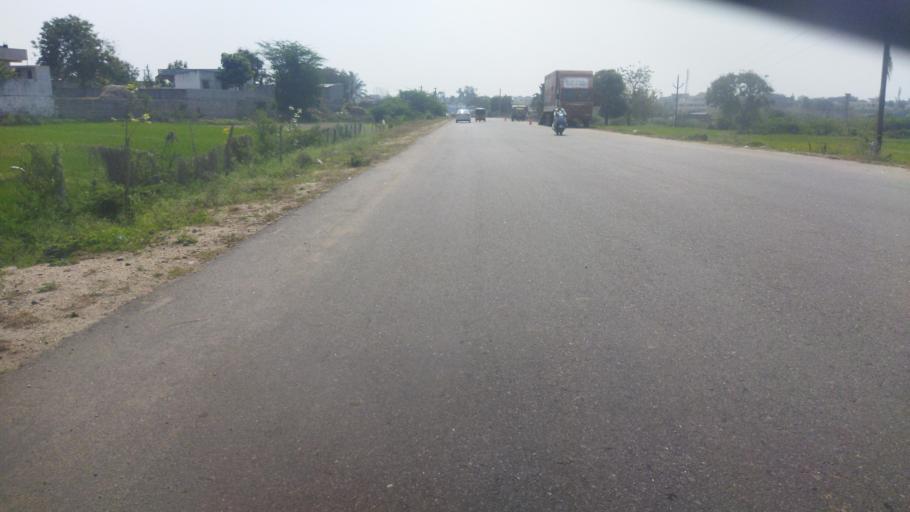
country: IN
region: Telangana
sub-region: Nalgonda
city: Nalgonda
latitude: 17.0777
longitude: 79.2836
